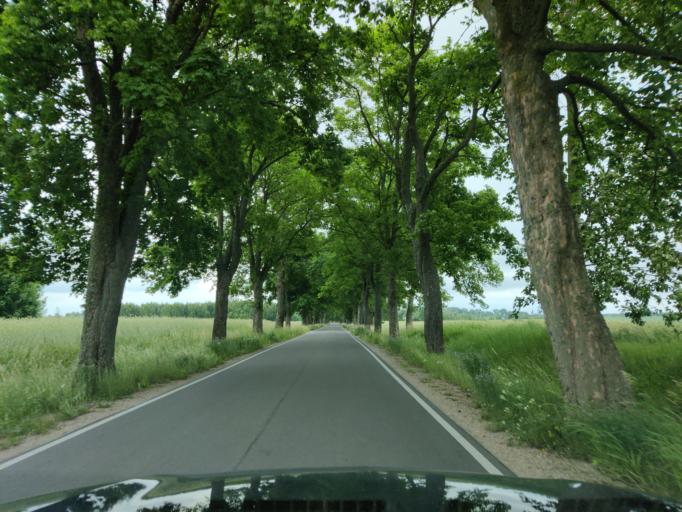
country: PL
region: Warmian-Masurian Voivodeship
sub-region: Powiat mragowski
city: Mikolajki
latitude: 53.8580
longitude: 21.6087
